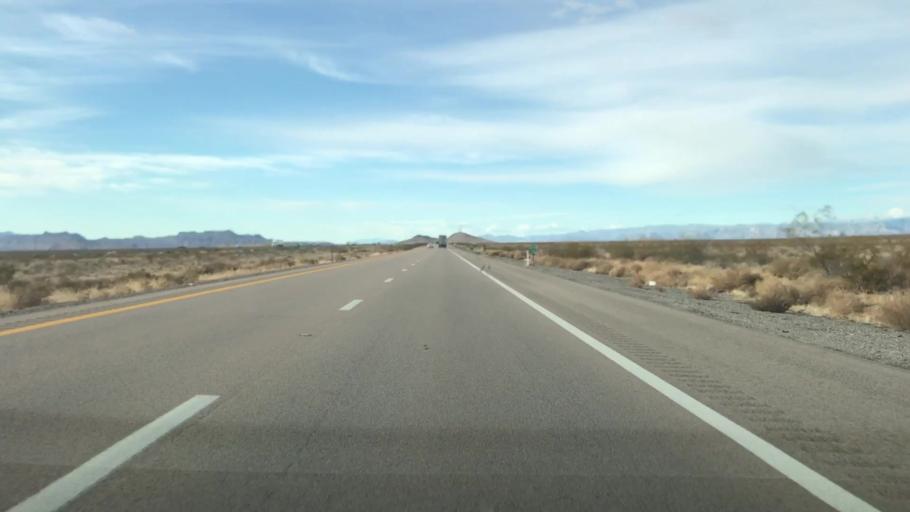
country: US
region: Nevada
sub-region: Clark County
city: Moapa Town
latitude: 36.7138
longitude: -114.4720
